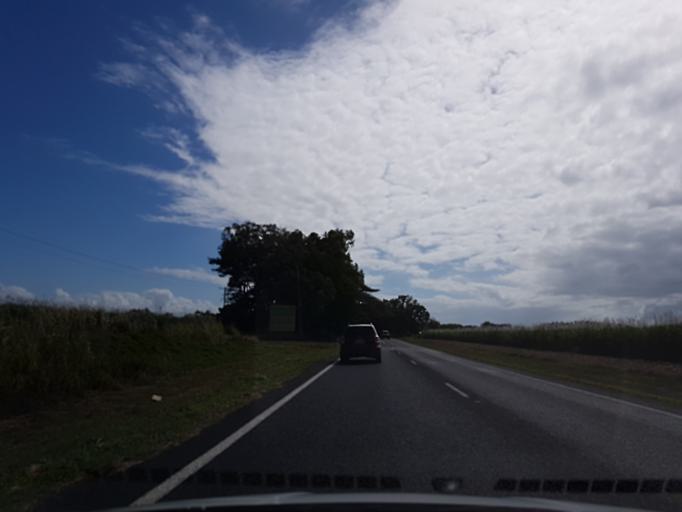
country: AU
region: Queensland
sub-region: Cairns
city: Port Douglas
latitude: -16.5445
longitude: 145.4714
